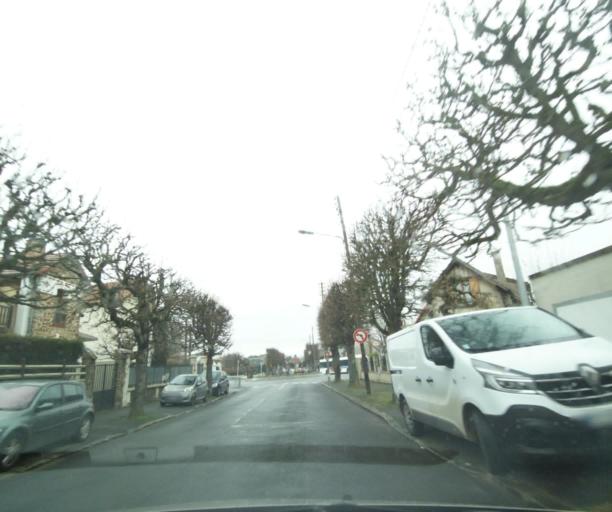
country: FR
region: Ile-de-France
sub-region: Departement du Val-de-Marne
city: Ablon-sur-Seine
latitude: 48.7338
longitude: 2.4160
